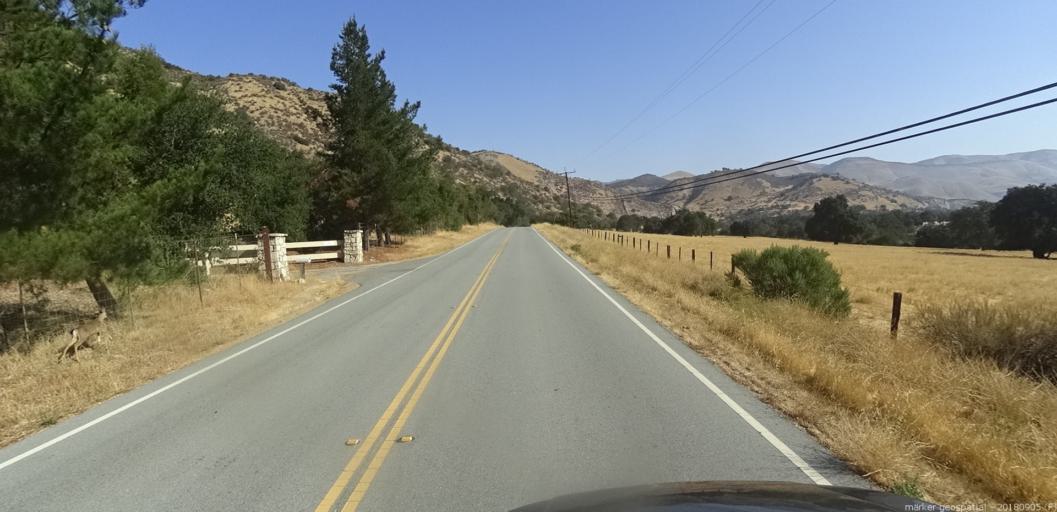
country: US
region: California
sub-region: Monterey County
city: Greenfield
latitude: 36.2470
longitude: -121.4323
